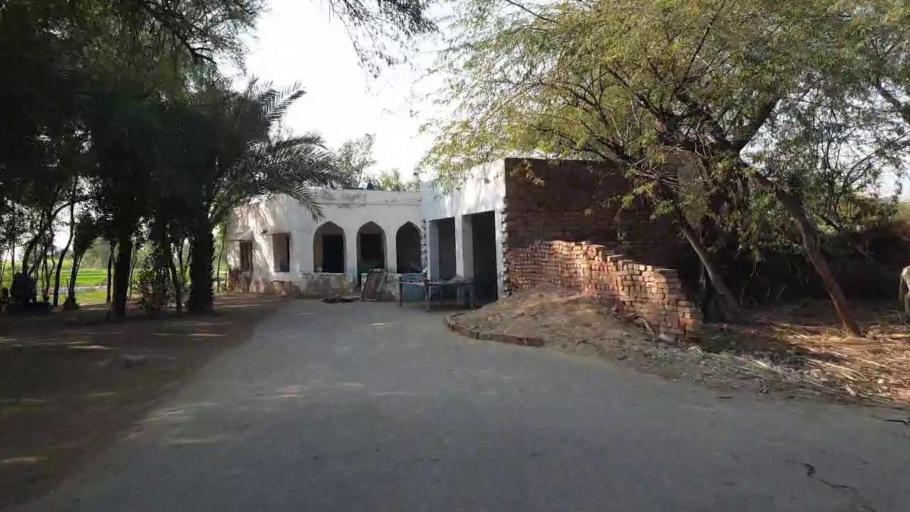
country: PK
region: Sindh
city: Tando Allahyar
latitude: 25.5929
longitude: 68.6178
